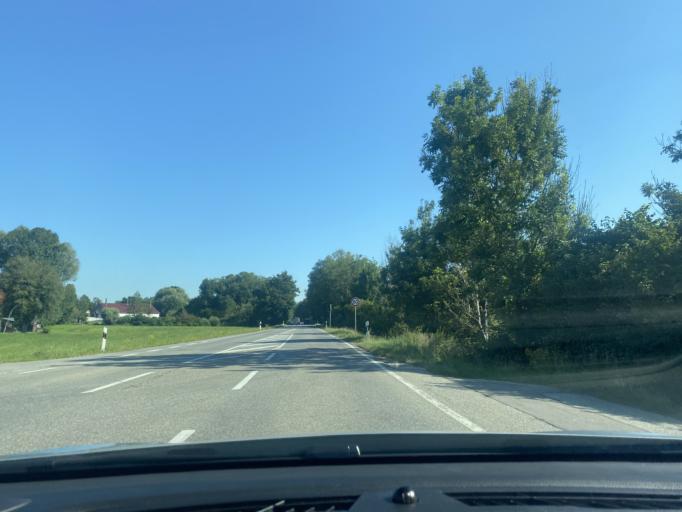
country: DE
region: Bavaria
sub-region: Upper Bavaria
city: Eitting
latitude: 48.3515
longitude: 11.8983
